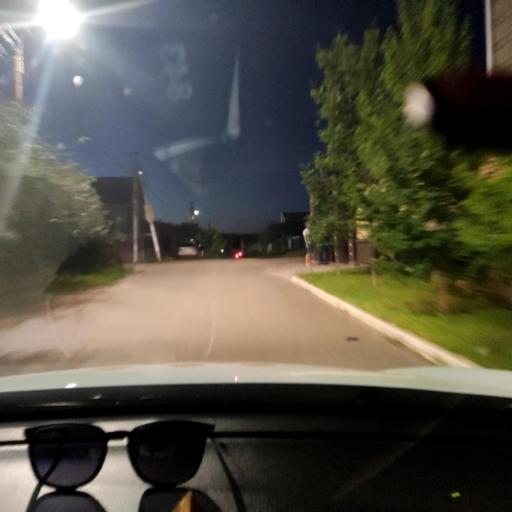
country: RU
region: Tatarstan
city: Verkhniy Uslon
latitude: 55.7986
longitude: 49.0322
